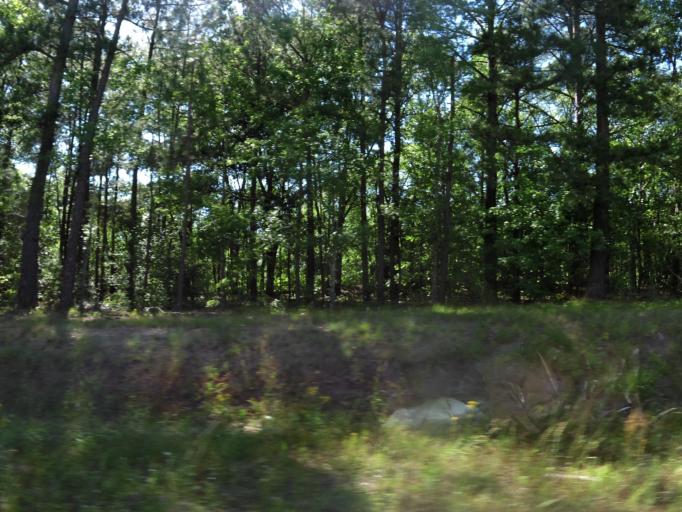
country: US
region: South Carolina
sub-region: Bamberg County
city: Denmark
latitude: 33.2855
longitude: -81.1494
